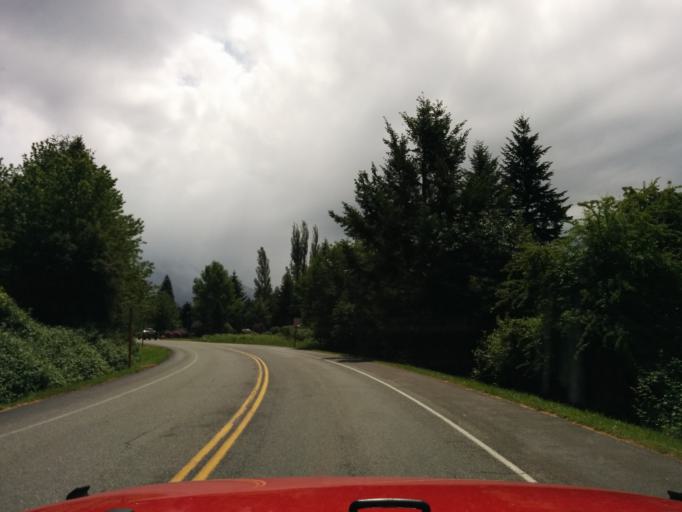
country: US
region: Washington
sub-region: King County
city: North Bend
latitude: 47.4900
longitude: -121.7788
